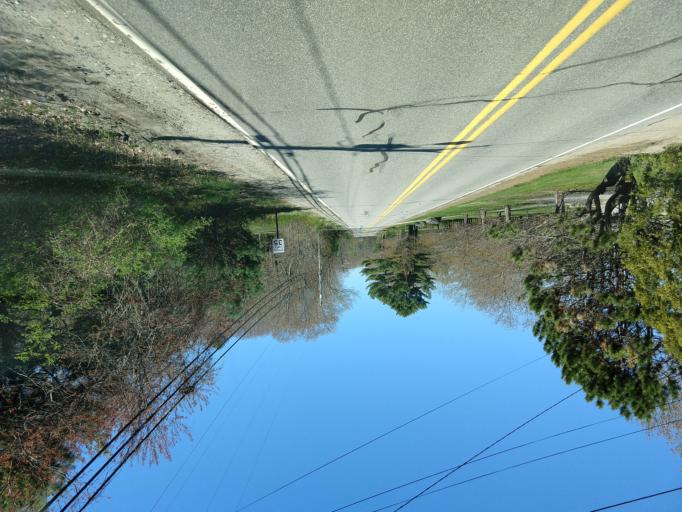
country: US
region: Maine
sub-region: York County
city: Old Orchard Beach
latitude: 43.4400
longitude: -70.3780
